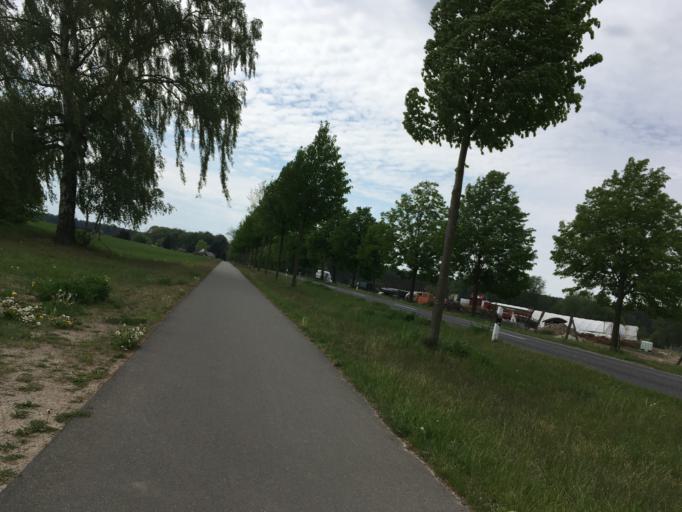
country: DE
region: Brandenburg
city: Rudnitz
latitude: 52.7175
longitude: 13.6217
